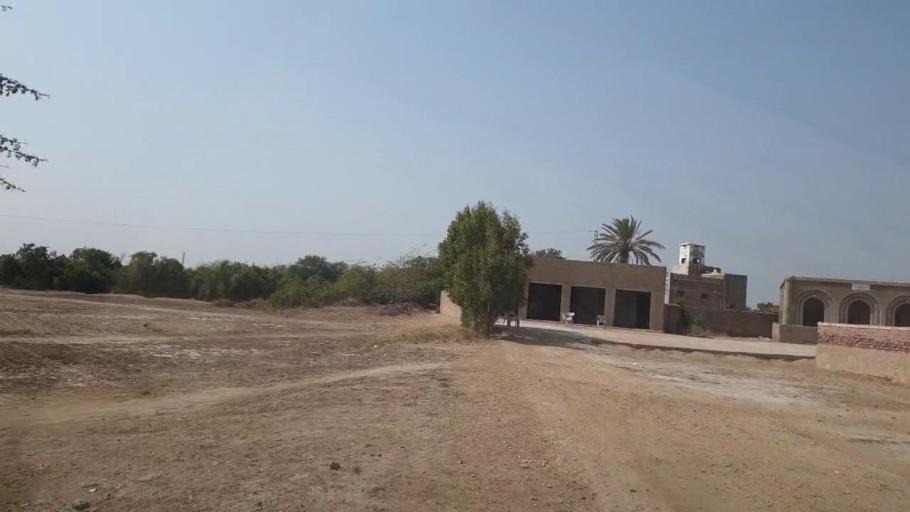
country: PK
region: Sindh
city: Mirpur Khas
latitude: 25.6479
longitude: 69.1271
